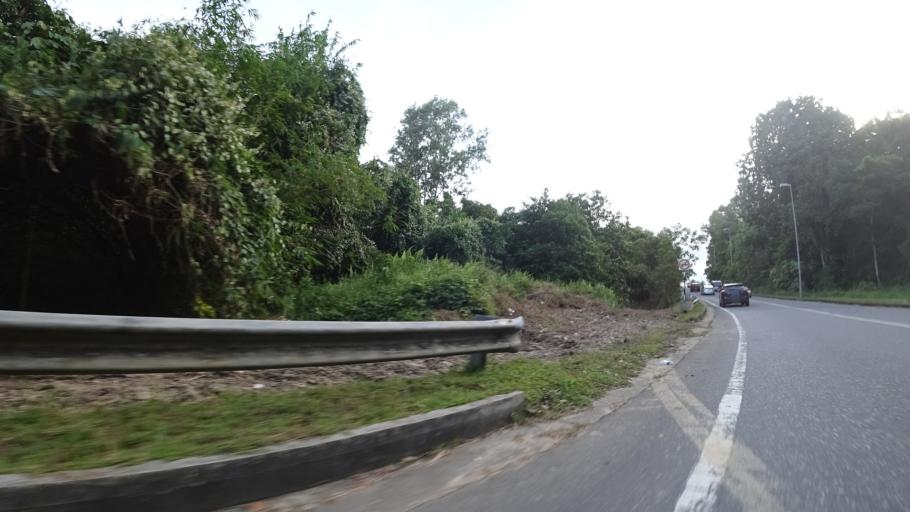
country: BN
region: Brunei and Muara
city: Bandar Seri Begawan
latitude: 4.8911
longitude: 114.9099
